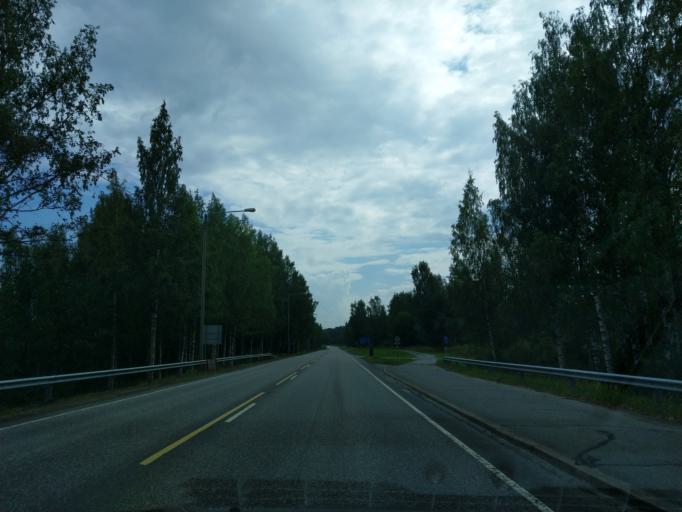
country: FI
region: South Karelia
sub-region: Imatra
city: Parikkala
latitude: 61.5999
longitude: 29.4830
